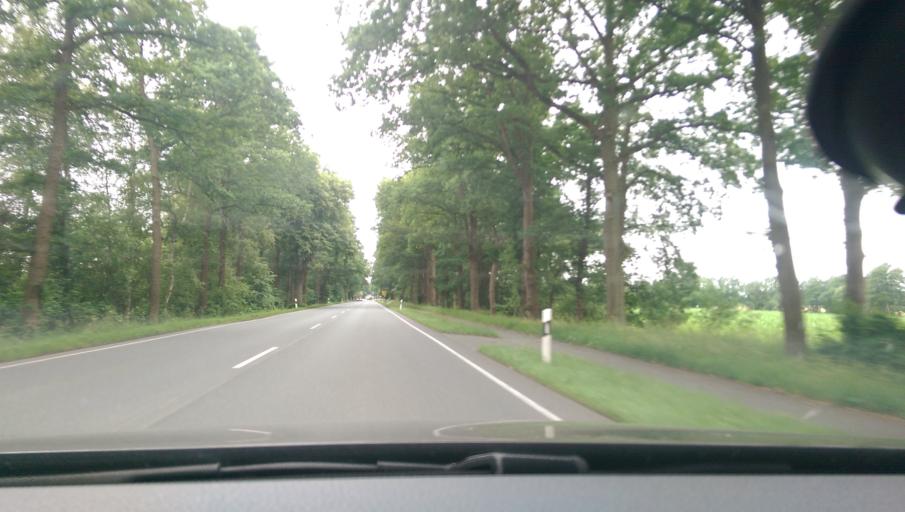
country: DE
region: Lower Saxony
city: Ahausen
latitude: 53.0503
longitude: 9.3303
